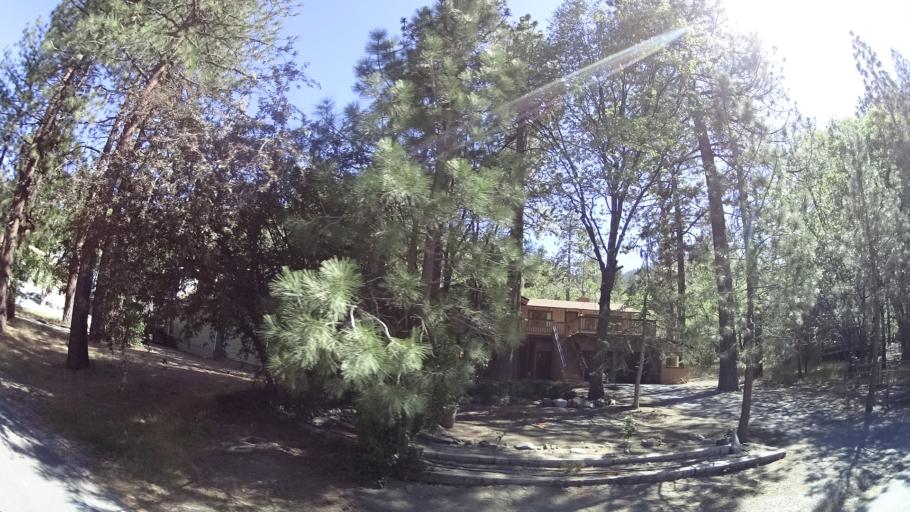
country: US
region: California
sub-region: San Bernardino County
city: Wrightwood
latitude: 34.3628
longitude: -117.6487
